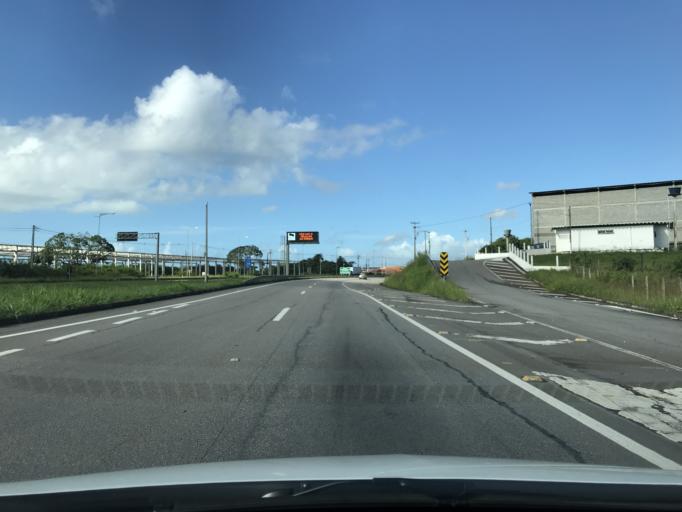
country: BR
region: Pernambuco
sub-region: Cabo De Santo Agostinho
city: Cabo
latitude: -8.3381
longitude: -35.0004
